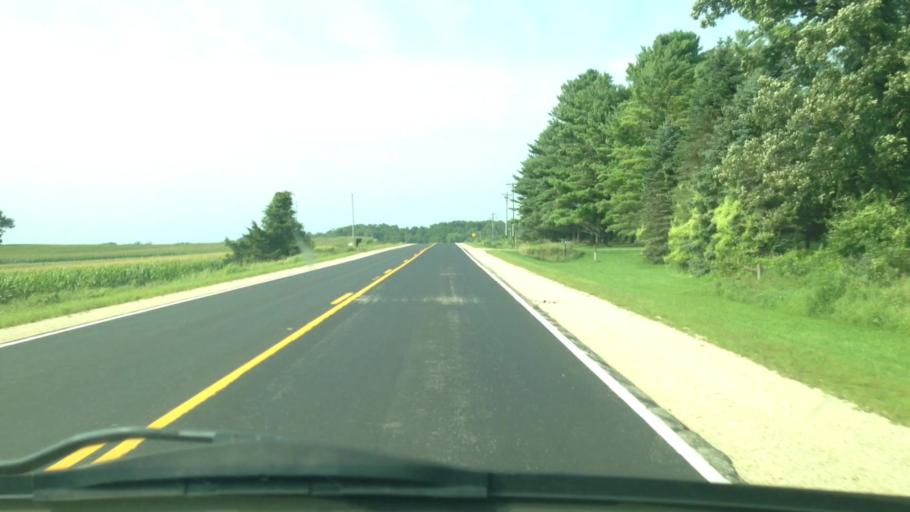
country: US
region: Minnesota
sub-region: Winona County
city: Lewiston
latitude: 43.9174
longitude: -91.9593
